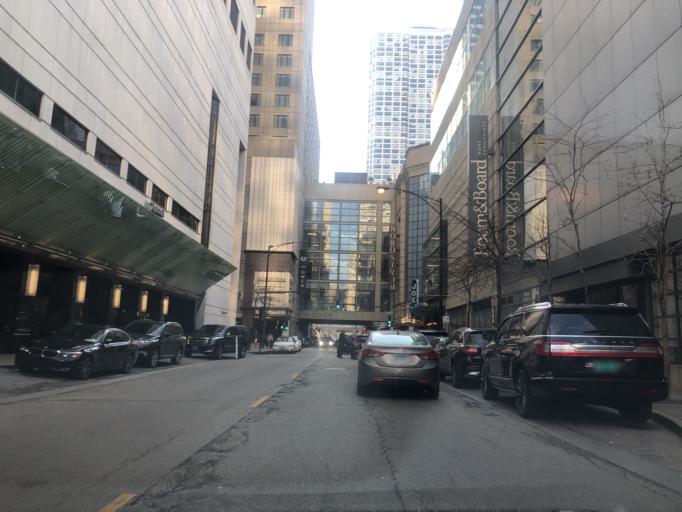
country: US
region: Illinois
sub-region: Cook County
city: Chicago
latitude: 41.8923
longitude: -87.6255
